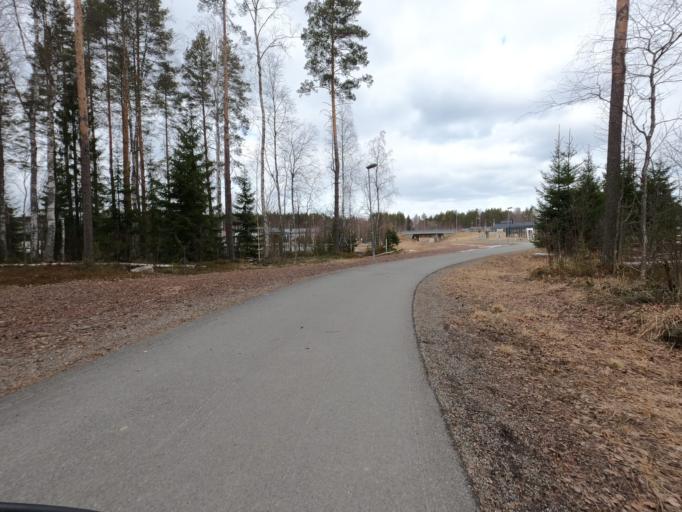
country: FI
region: North Karelia
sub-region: Joensuu
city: Joensuu
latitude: 62.5699
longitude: 29.8130
